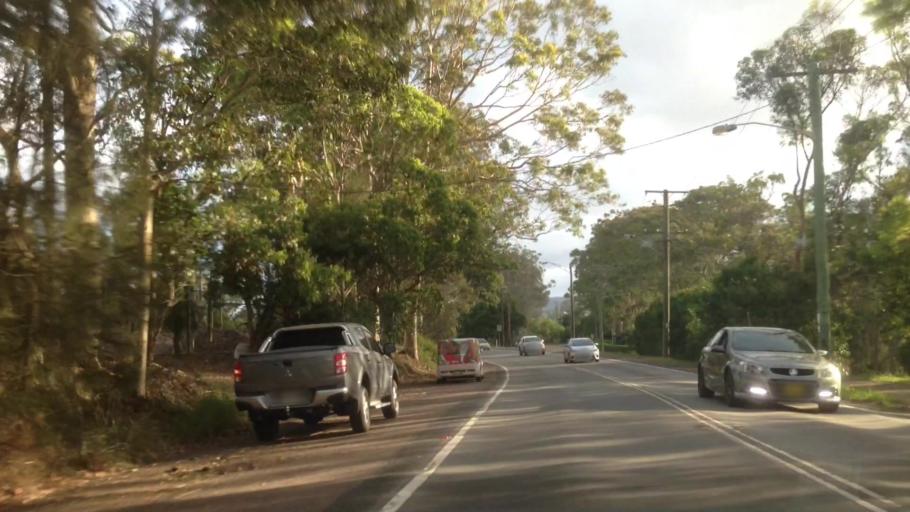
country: AU
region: New South Wales
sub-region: Wyong Shire
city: Chittaway Bay
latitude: -33.2879
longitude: 151.4243
